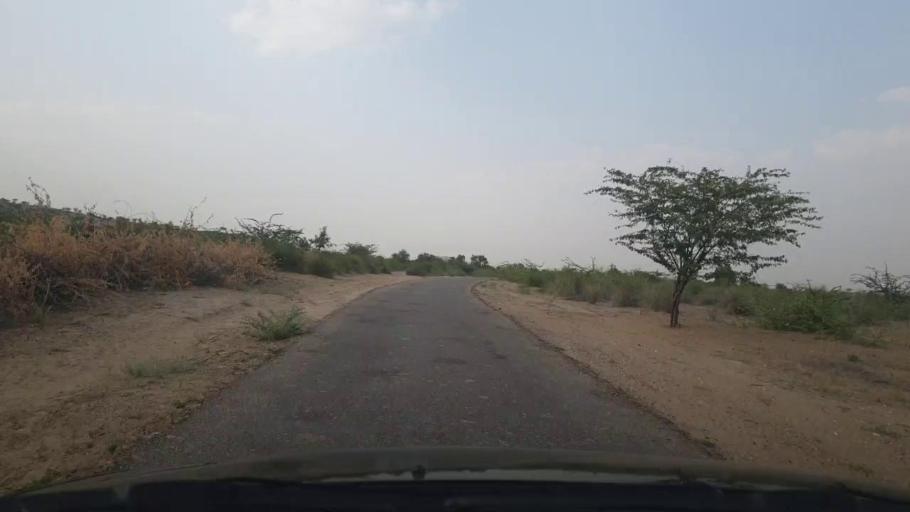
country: PK
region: Sindh
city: Islamkot
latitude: 25.0339
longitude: 70.5548
